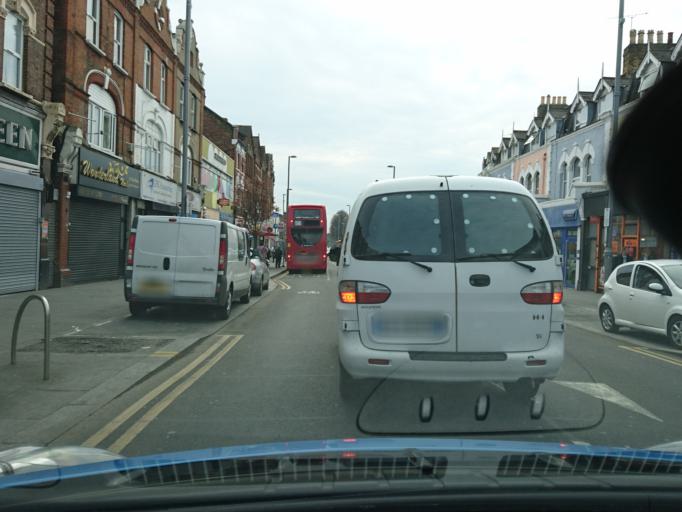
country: GB
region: England
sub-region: Greater London
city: Walthamstow
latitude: 51.5760
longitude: -0.0118
